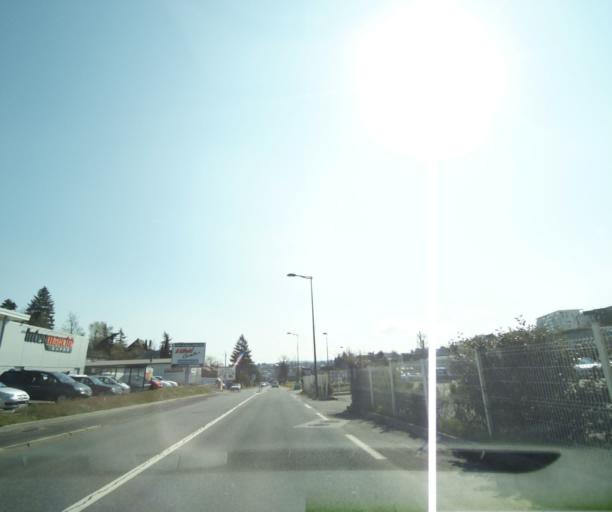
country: FR
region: Midi-Pyrenees
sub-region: Departement de l'Aveyron
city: Olemps
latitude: 44.3636
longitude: 2.5550
